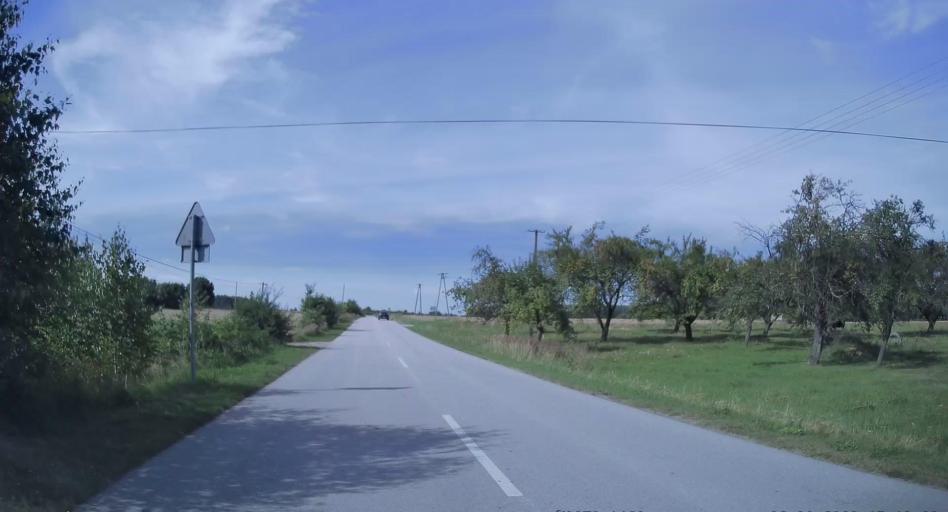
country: PL
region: Lodz Voivodeship
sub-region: Powiat opoczynski
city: Mniszkow
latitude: 51.3572
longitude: 20.0370
